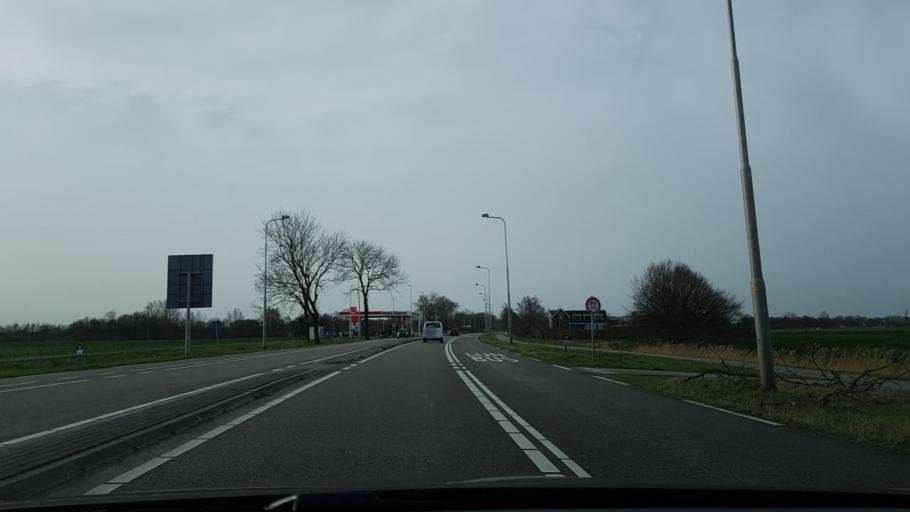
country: NL
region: North Holland
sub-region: Gemeente Ouder-Amstel
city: Ouderkerk aan de Amstel
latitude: 52.3062
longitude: 4.9243
